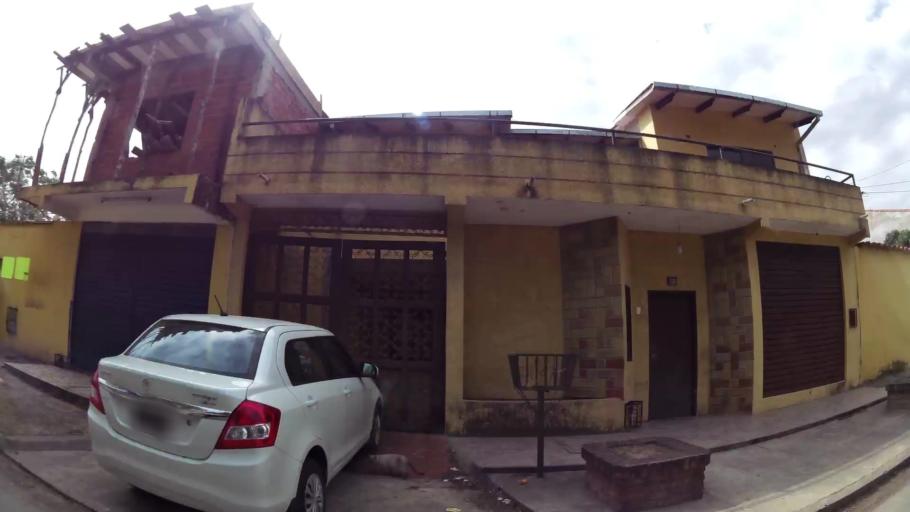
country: BO
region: Santa Cruz
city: Santa Cruz de la Sierra
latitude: -17.7741
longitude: -63.2085
